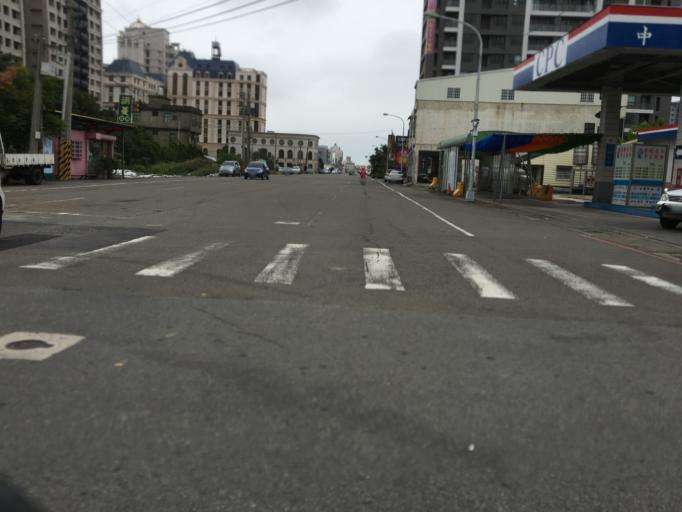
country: TW
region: Taiwan
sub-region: Hsinchu
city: Hsinchu
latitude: 24.6918
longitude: 120.8930
